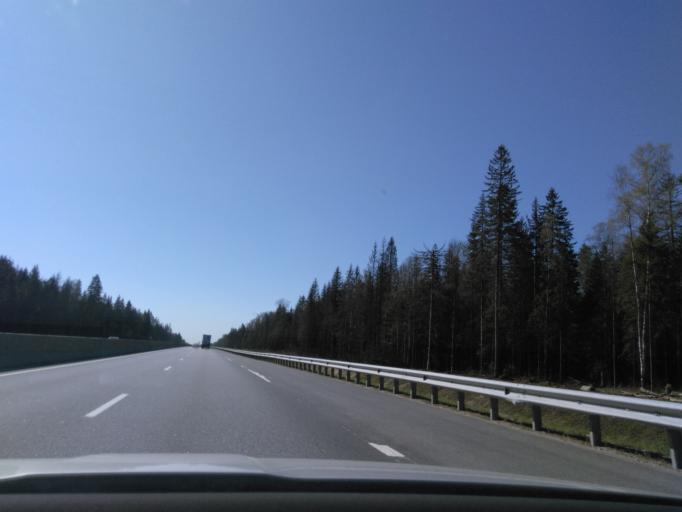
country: RU
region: Moskovskaya
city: Rzhavki
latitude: 56.0246
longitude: 37.2740
